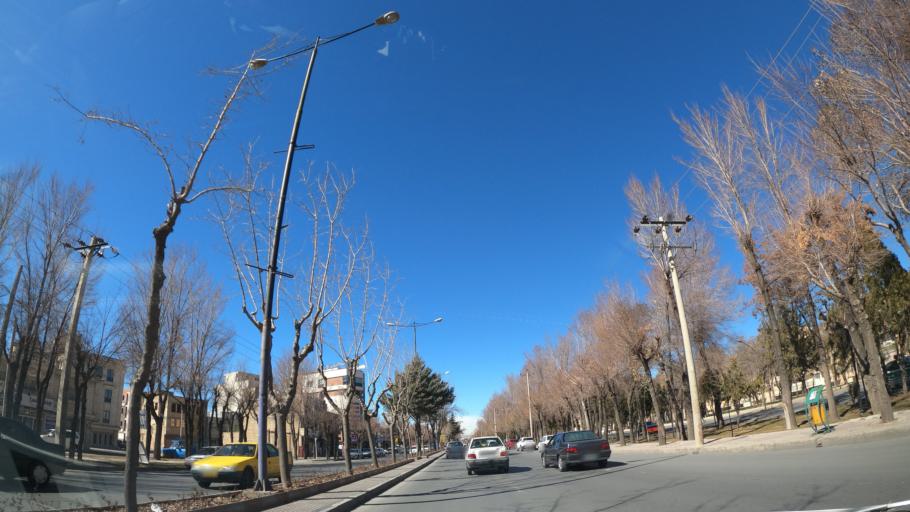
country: IR
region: Chahar Mahall va Bakhtiari
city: Shahrekord
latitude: 32.3127
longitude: 50.8804
